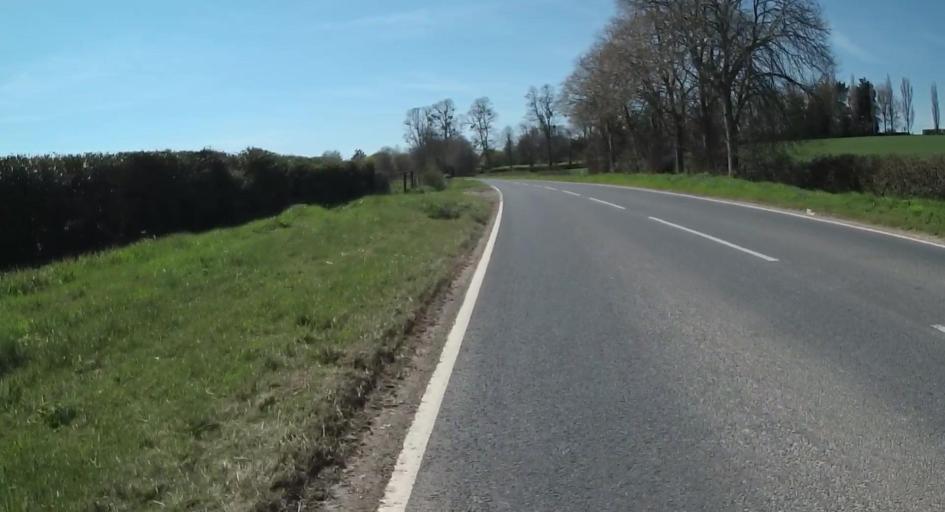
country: GB
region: England
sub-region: Hampshire
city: Chandlers Ford
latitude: 51.0943
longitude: -1.4311
